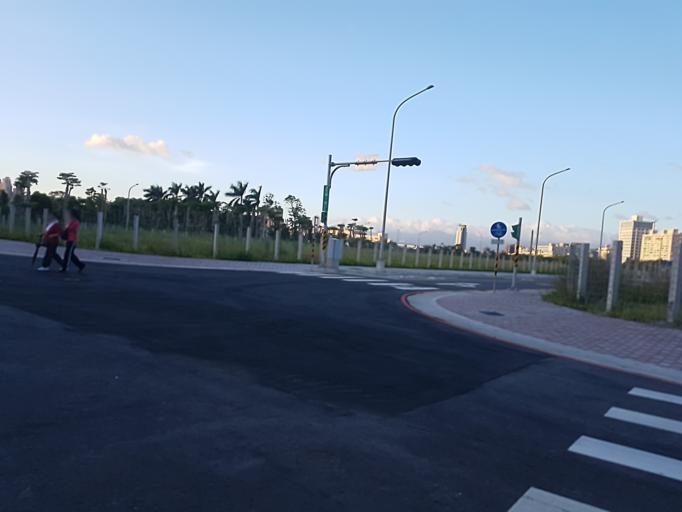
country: TW
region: Taipei
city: Taipei
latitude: 24.9760
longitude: 121.5296
